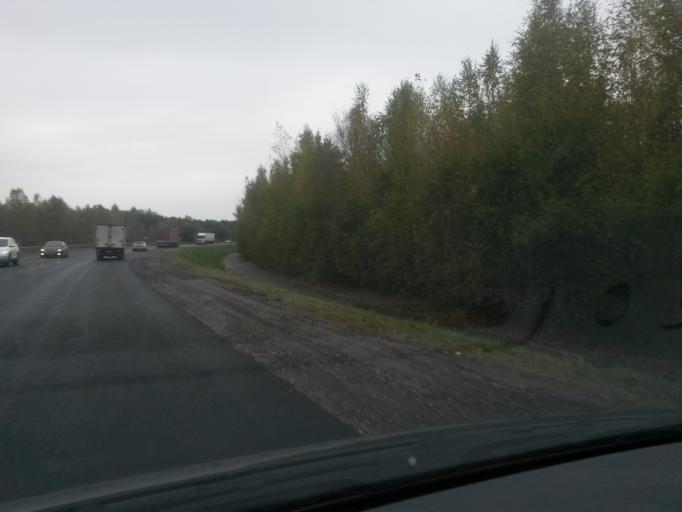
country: RU
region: Nizjnij Novgorod
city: Pamyat' Parizhskoy Kommuny
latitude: 56.0781
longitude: 44.3680
